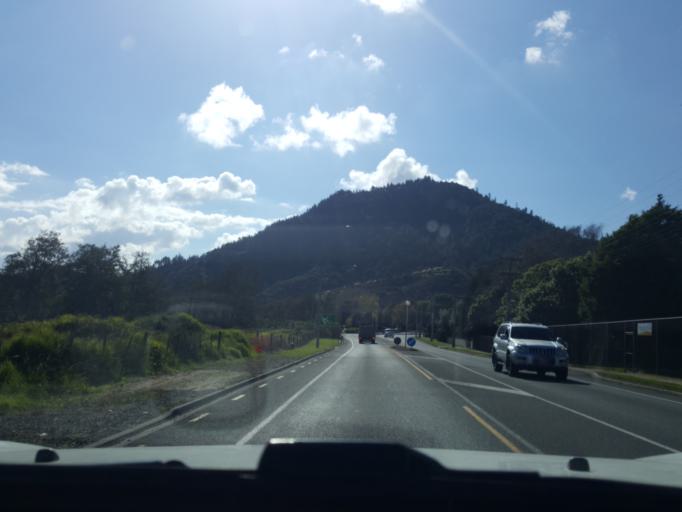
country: NZ
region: Waikato
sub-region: Waikato District
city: Ngaruawahia
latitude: -37.6143
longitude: 175.1865
